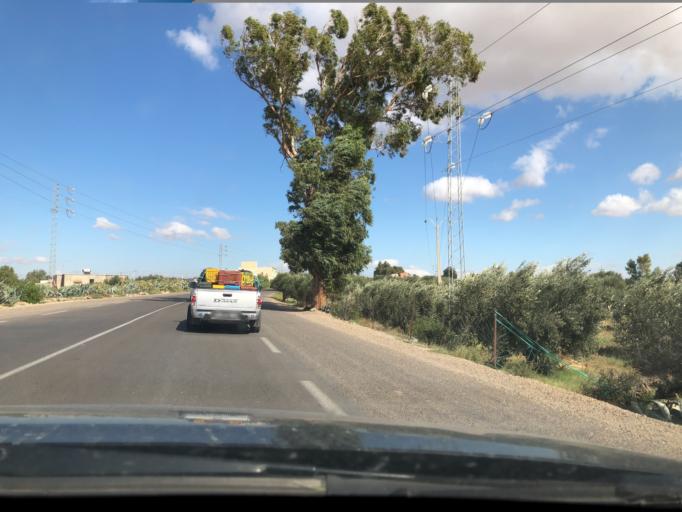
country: TN
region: Al Qasrayn
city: Kasserine
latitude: 35.2043
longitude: 8.8804
